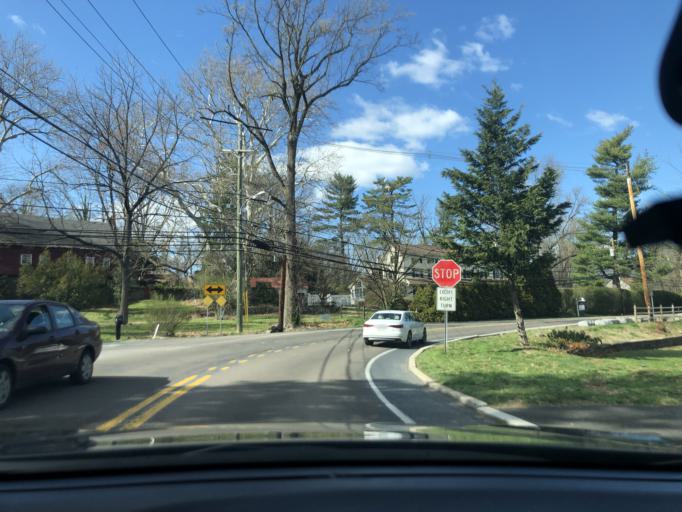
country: US
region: Pennsylvania
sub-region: Montgomery County
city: Blue Bell
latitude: 40.1437
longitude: -75.2738
